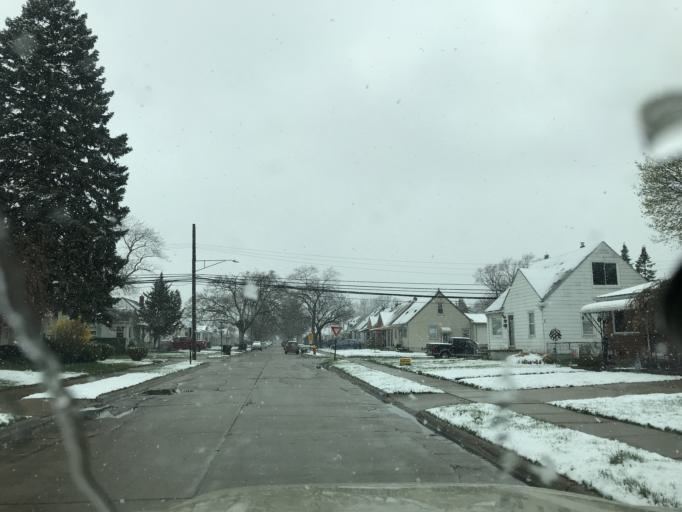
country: US
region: Michigan
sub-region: Wayne County
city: Allen Park
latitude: 42.2631
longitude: -83.1935
